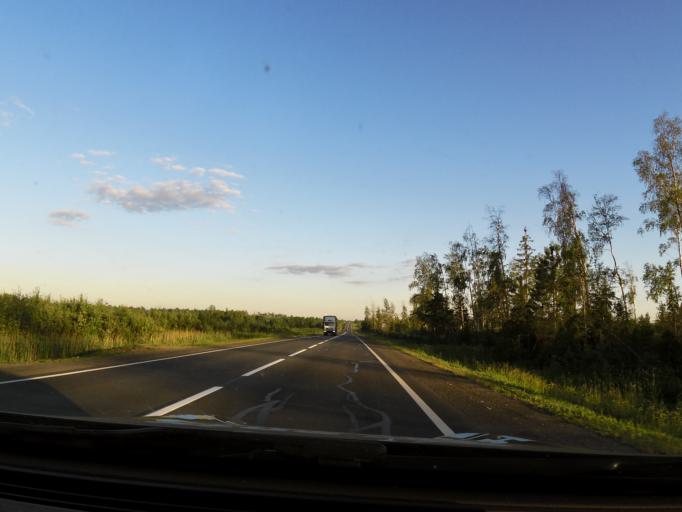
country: RU
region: Jaroslavl
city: Prechistoye
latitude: 58.6024
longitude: 40.3406
